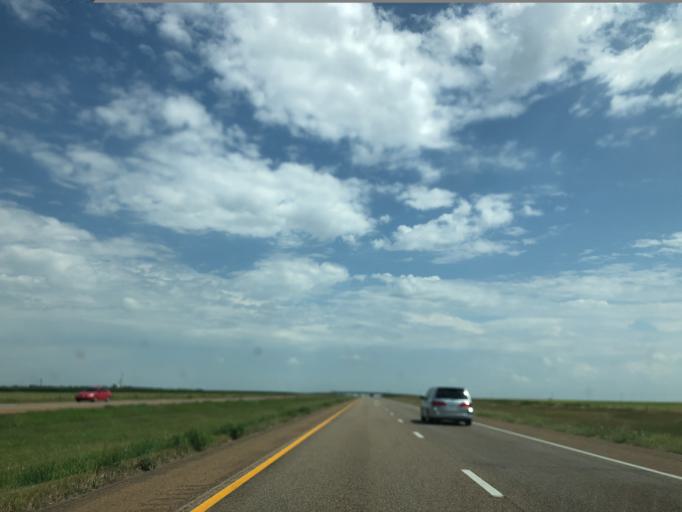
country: US
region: Kansas
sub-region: Thomas County
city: Colby
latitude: 39.3281
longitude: -100.9997
